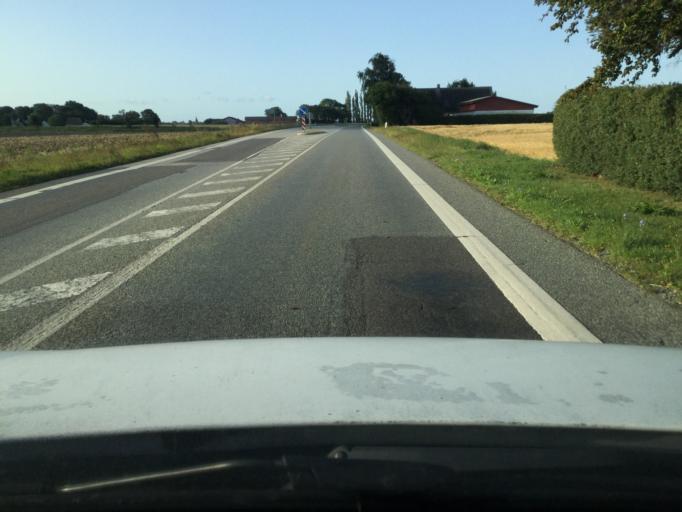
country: DK
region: Zealand
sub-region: Lolland Kommune
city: Rodby
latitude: 54.7138
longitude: 11.3823
